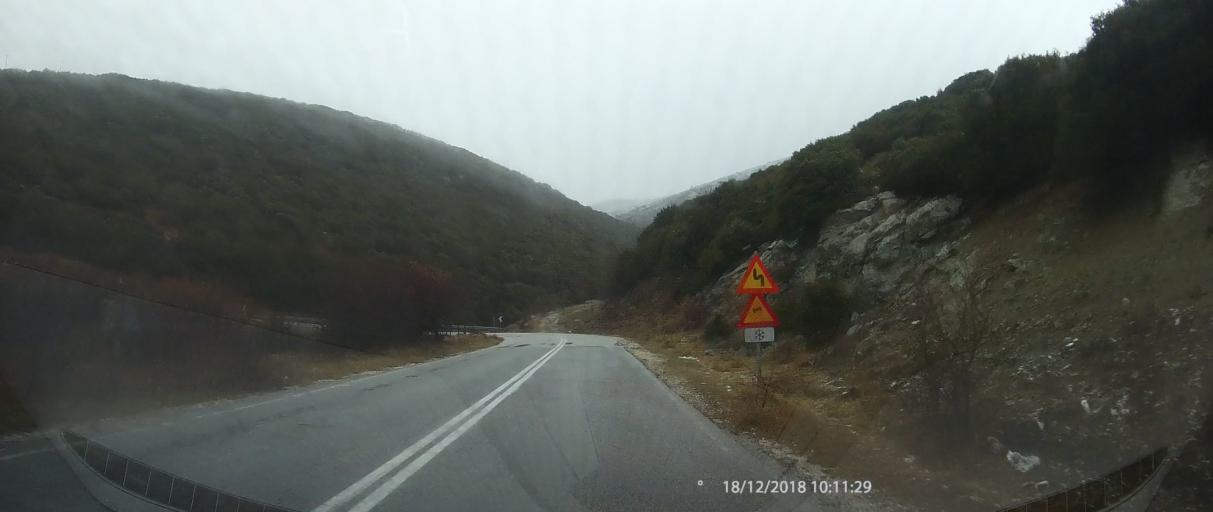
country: GR
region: Thessaly
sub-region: Nomos Larisis
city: Livadi
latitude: 40.0930
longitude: 22.2103
